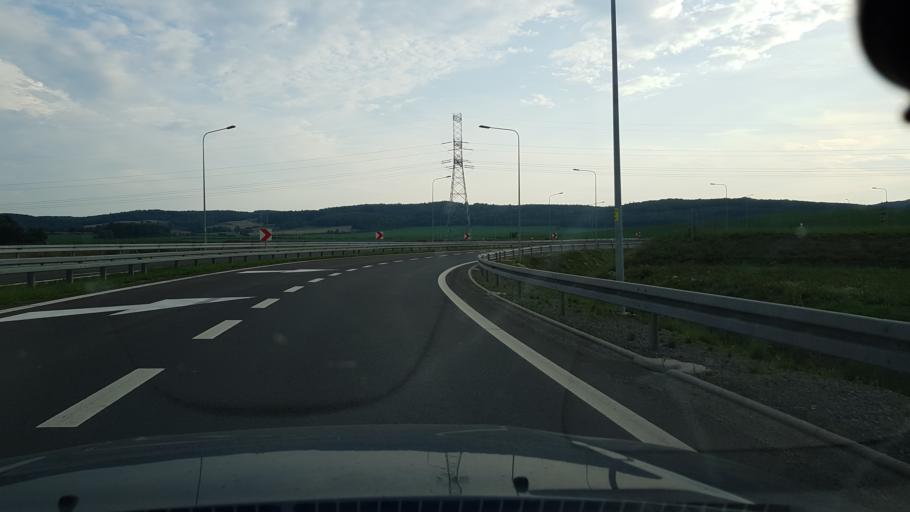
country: PL
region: Lower Silesian Voivodeship
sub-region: Powiat jaworski
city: Bolkow
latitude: 50.9104
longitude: 16.1571
